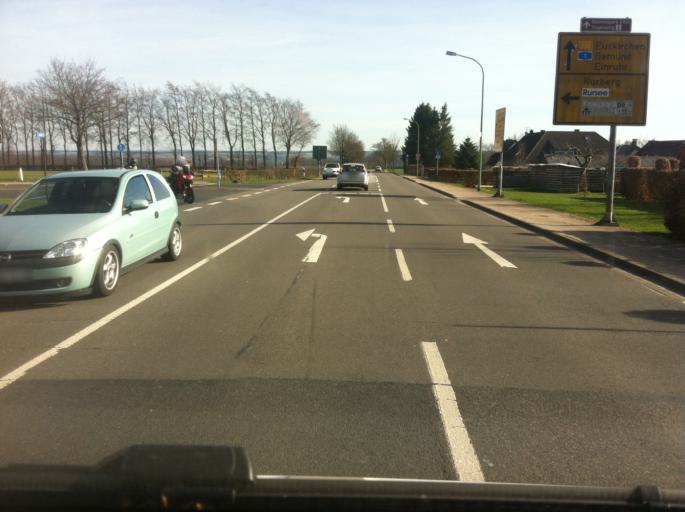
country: DE
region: North Rhine-Westphalia
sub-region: Regierungsbezirk Koln
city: Simmerath
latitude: 50.6031
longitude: 6.3397
